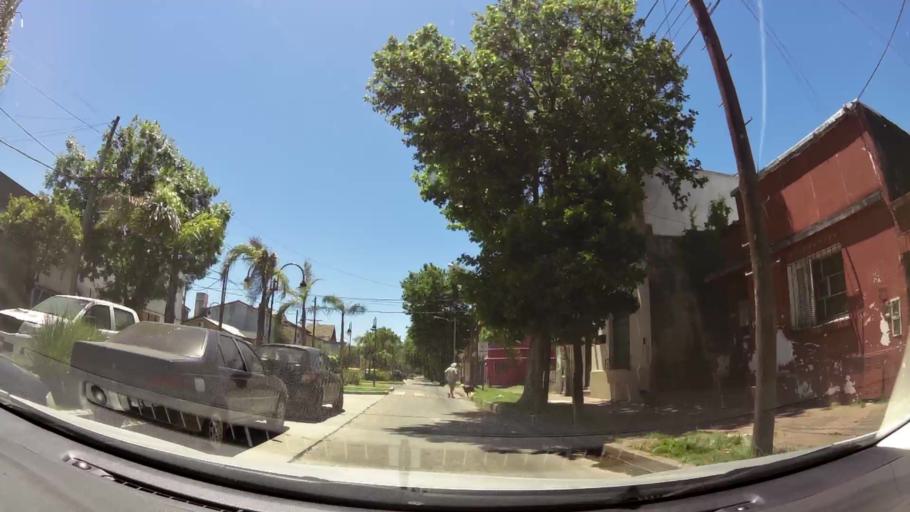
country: AR
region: Buenos Aires
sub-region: Partido de Tigre
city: Tigre
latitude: -34.4555
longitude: -58.5487
